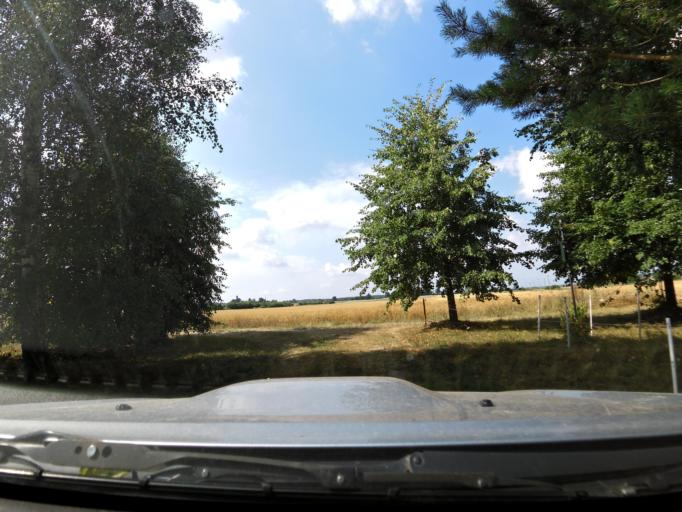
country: LT
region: Klaipedos apskritis
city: Silute
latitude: 55.4740
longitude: 21.4690
